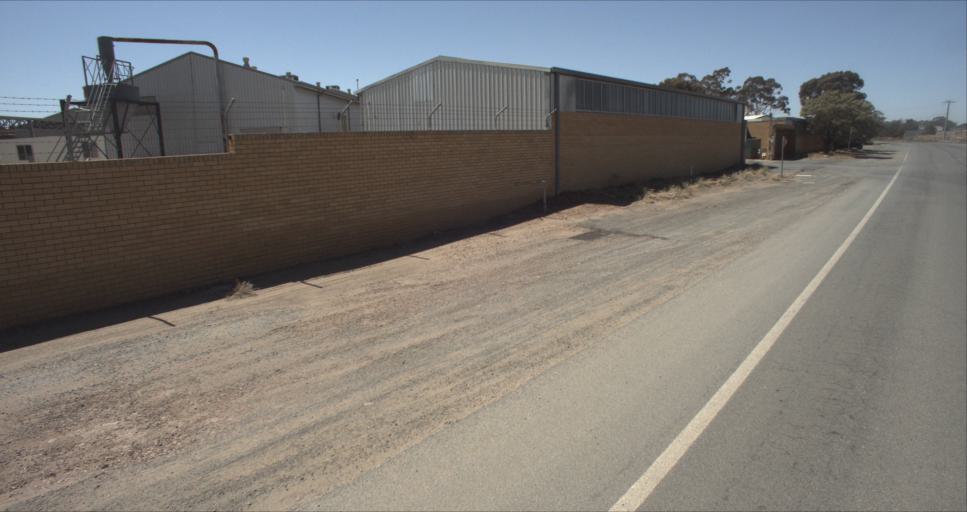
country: AU
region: New South Wales
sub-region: Leeton
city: Leeton
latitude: -34.5519
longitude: 146.3941
